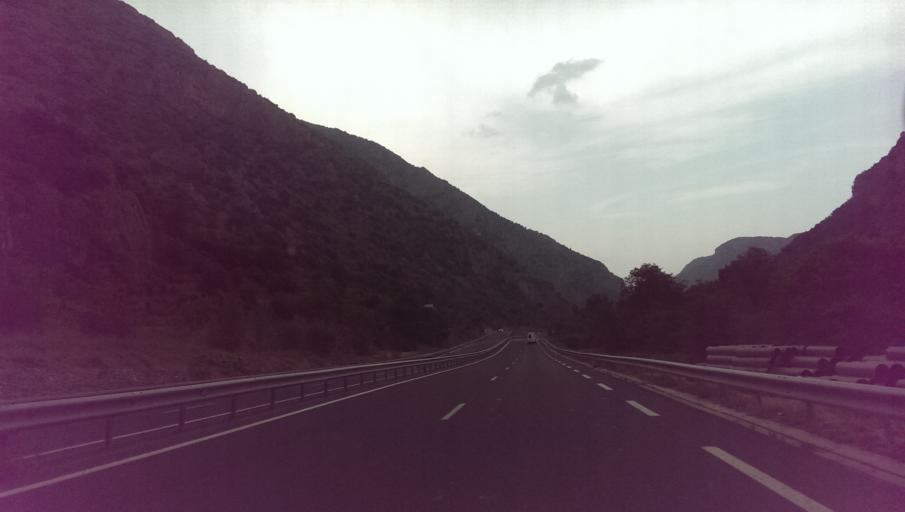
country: FR
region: Languedoc-Roussillon
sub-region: Departement des Pyrenees-Orientales
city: Vernet-les-Bains
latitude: 42.5754
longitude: 2.3420
